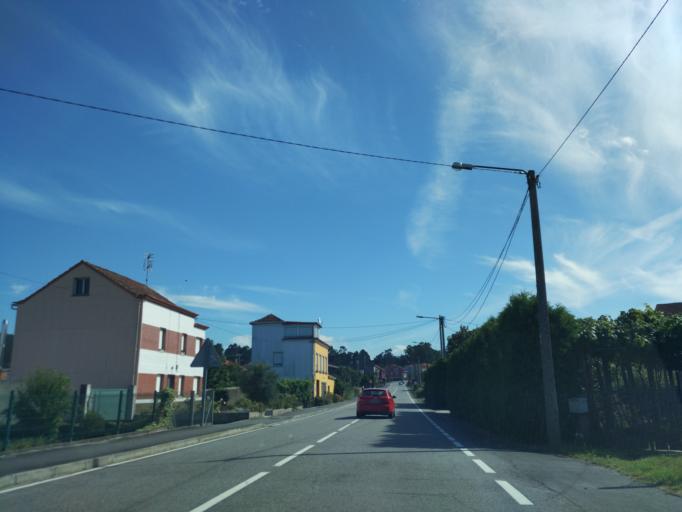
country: ES
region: Galicia
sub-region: Provincia da Coruna
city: Padron
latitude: 42.7185
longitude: -8.6855
